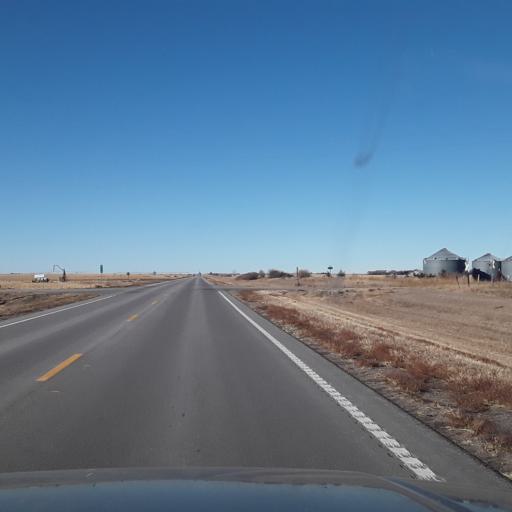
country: US
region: Nebraska
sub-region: Gosper County
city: Elwood
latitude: 40.5385
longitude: -99.6599
